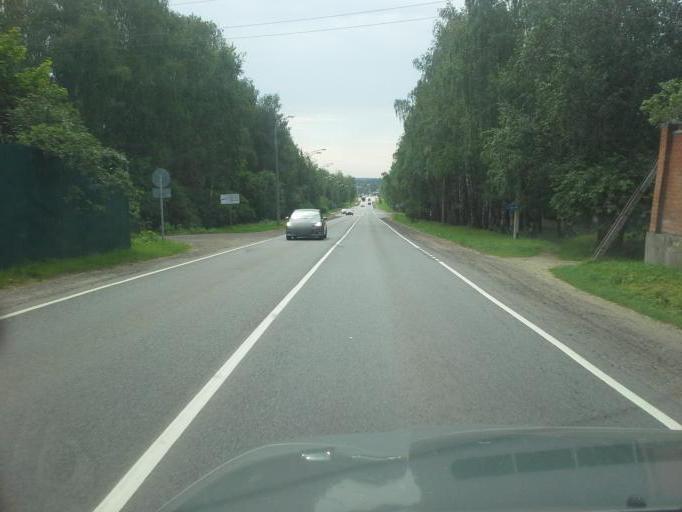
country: RU
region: Moskovskaya
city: Zhavoronki
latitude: 55.6020
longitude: 37.1086
